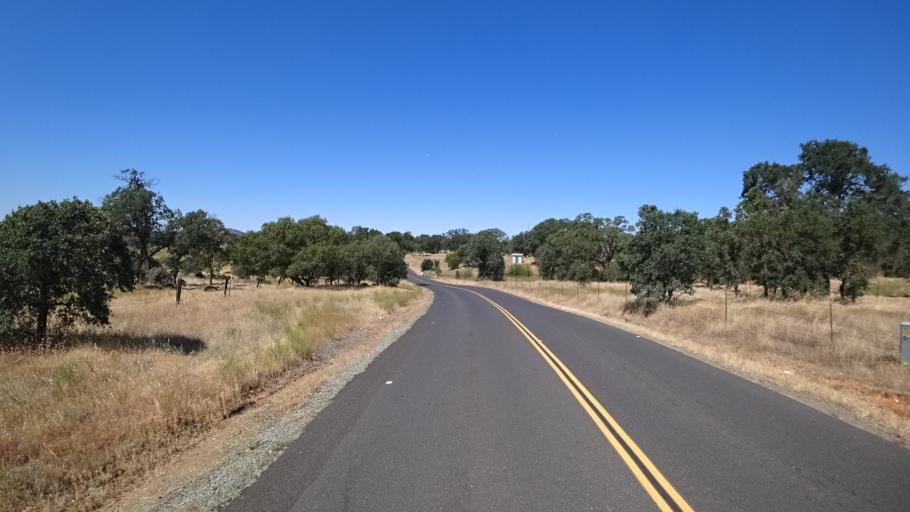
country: US
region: California
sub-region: Calaveras County
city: Copperopolis
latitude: 37.9741
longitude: -120.6467
